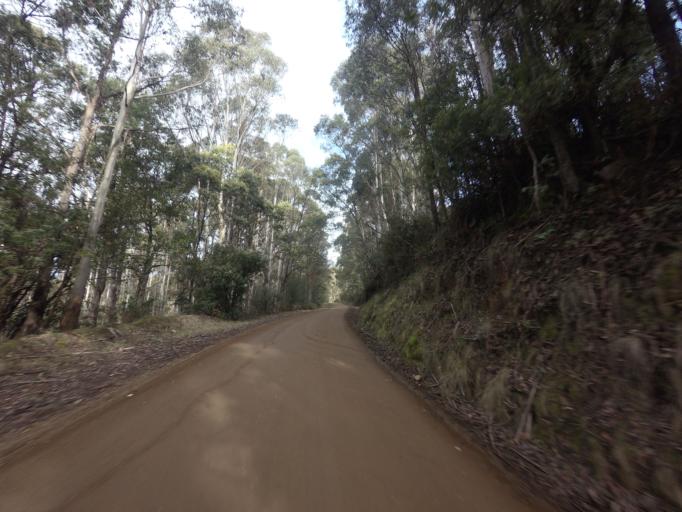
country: AU
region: Tasmania
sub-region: Derwent Valley
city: New Norfolk
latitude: -42.7884
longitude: 146.9350
